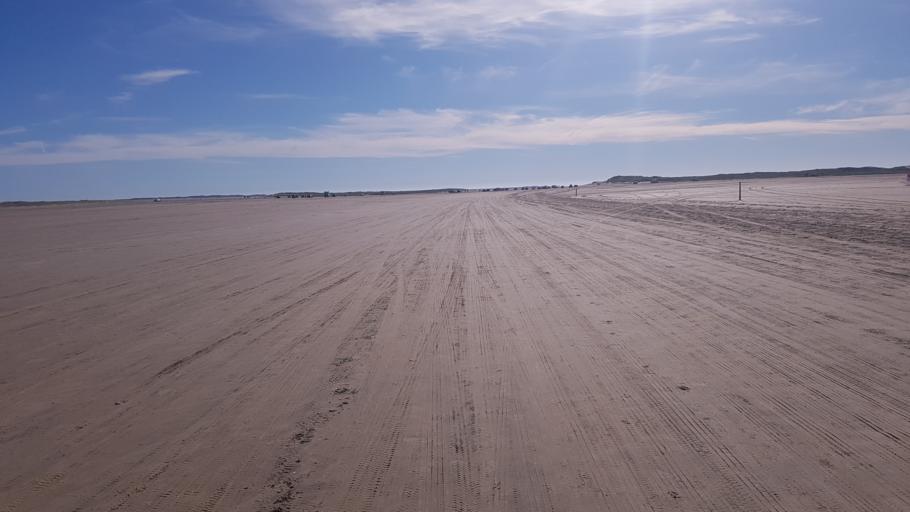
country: DE
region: Schleswig-Holstein
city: List
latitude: 55.0765
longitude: 8.5018
